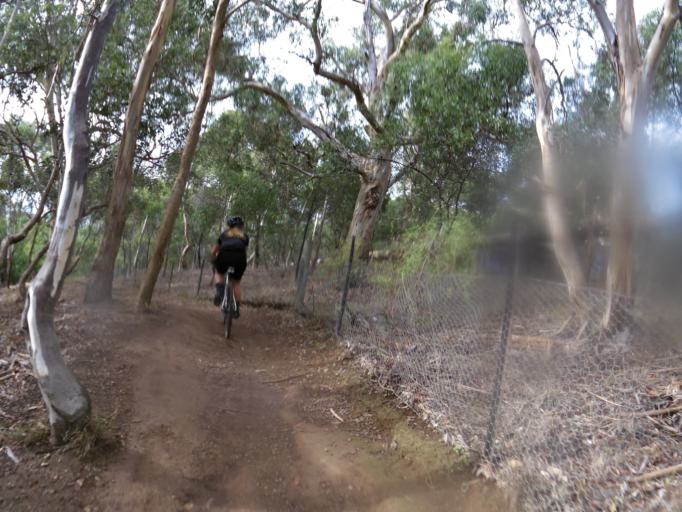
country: AU
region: Victoria
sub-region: Darebin
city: Fairfield
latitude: -37.7859
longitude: 145.0148
